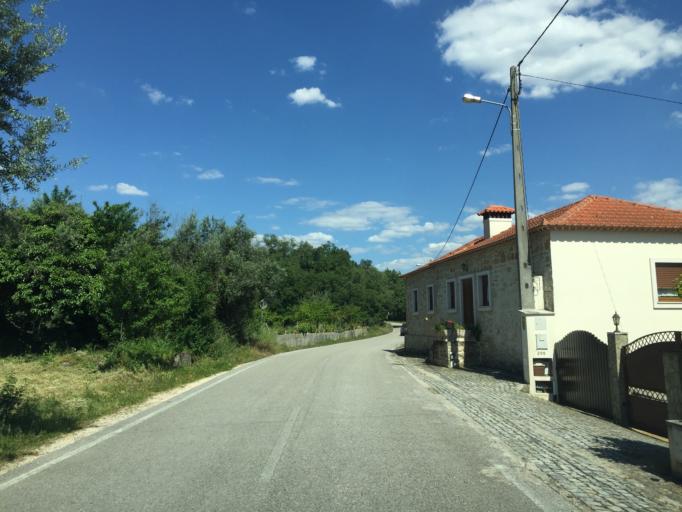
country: PT
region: Leiria
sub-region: Alvaiazere
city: Alvaiazere
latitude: 39.8034
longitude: -8.4083
